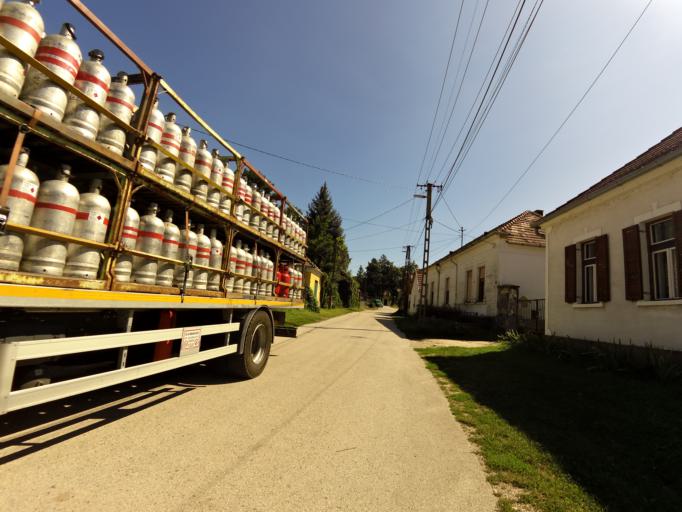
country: HU
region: Veszprem
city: Tapolca
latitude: 46.8330
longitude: 17.4326
